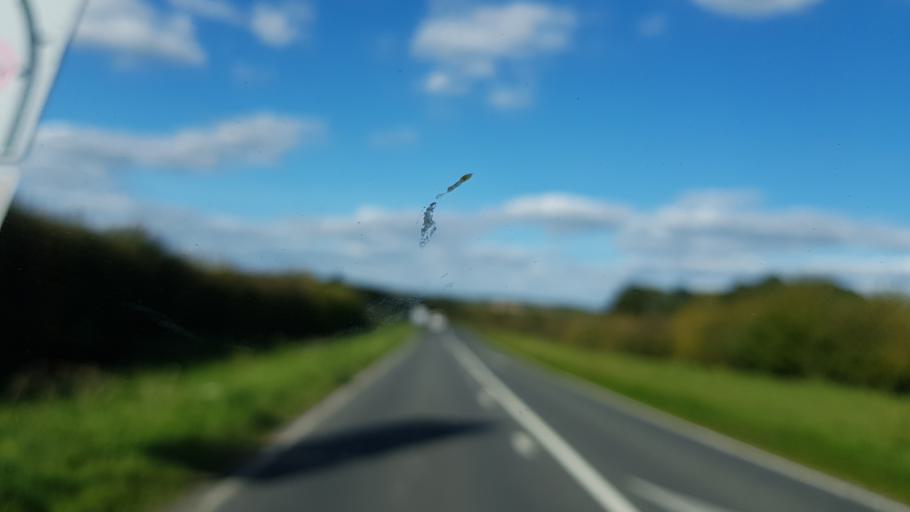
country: GB
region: England
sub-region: West Sussex
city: Petworth
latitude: 51.0413
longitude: -0.6406
